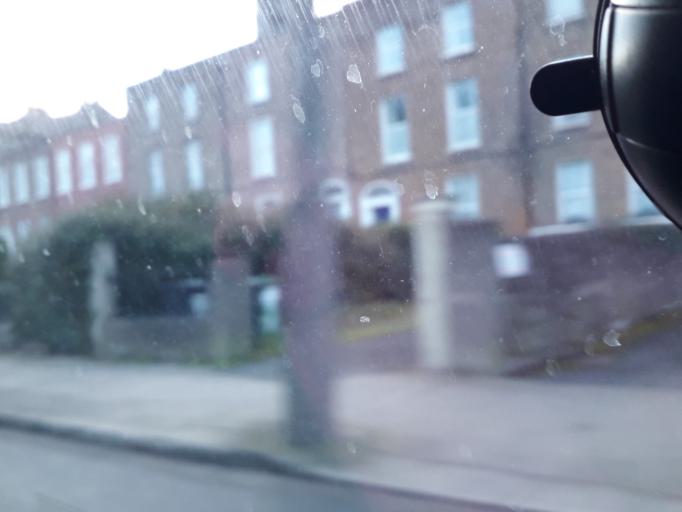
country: IE
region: Leinster
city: Rathgar
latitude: 53.3183
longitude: -6.2697
